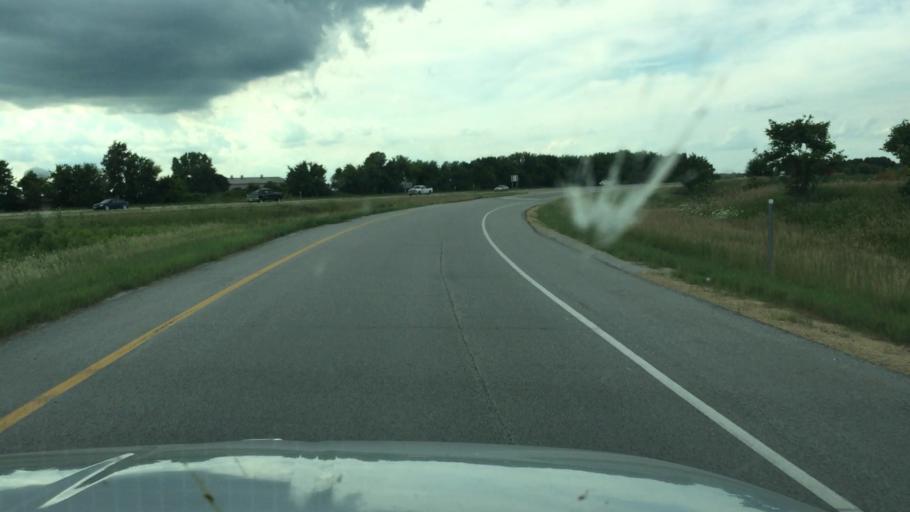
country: US
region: Iowa
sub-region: Scott County
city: Blue Grass
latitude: 41.5405
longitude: -90.6765
